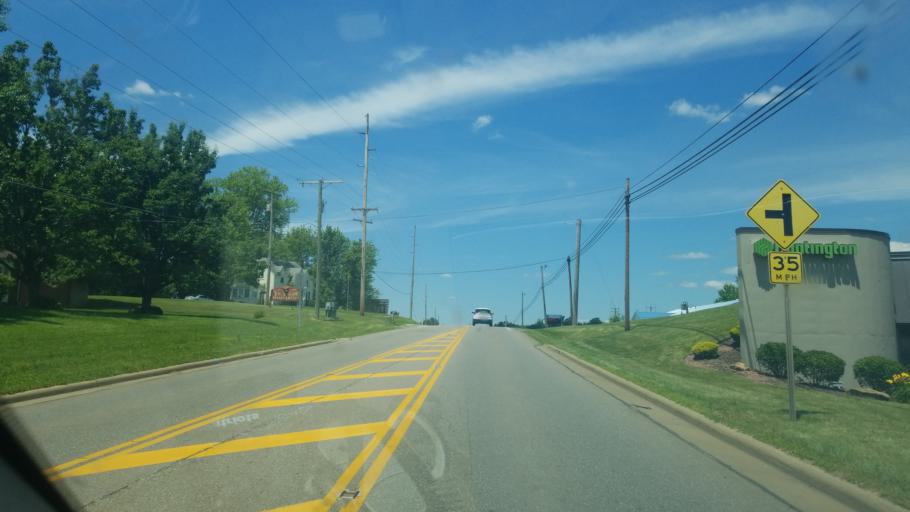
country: US
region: Ohio
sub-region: Columbiana County
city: Lisbon
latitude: 40.7926
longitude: -80.7789
